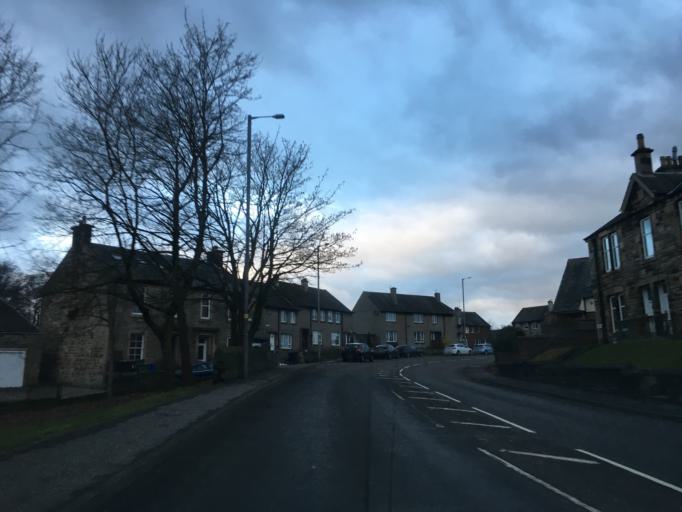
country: GB
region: Scotland
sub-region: Stirling
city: Bannockburn
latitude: 56.0929
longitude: -3.9194
